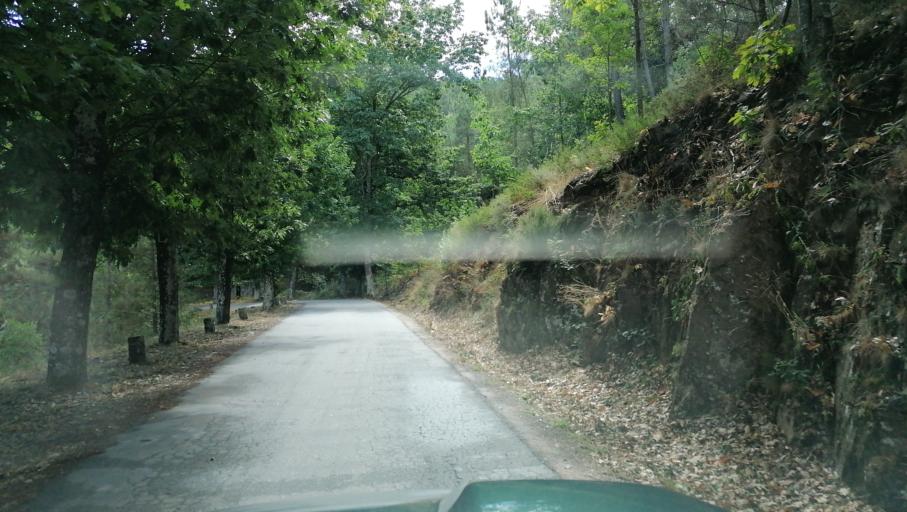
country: PT
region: Vila Real
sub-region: Vila Pouca de Aguiar
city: Vila Pouca de Aguiar
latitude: 41.5319
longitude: -7.5972
